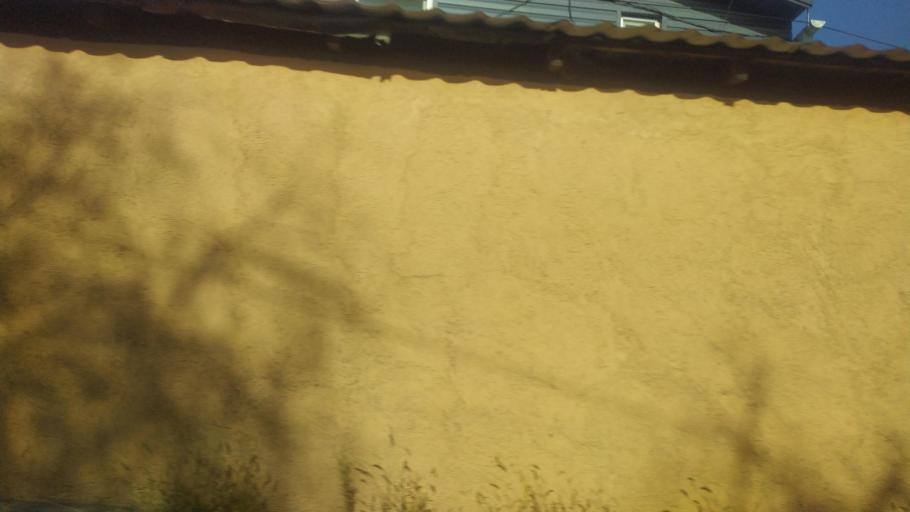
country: KZ
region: Almaty Qalasy
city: Almaty
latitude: 43.2655
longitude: 76.8741
